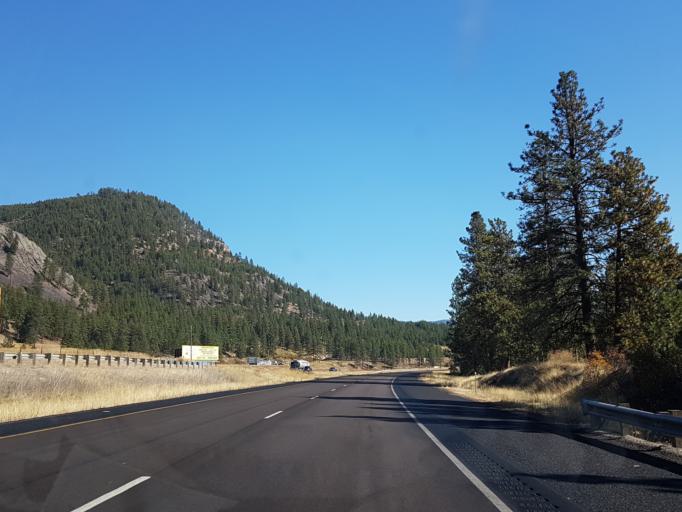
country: US
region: Montana
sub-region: Missoula County
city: Frenchtown
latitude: 47.0179
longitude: -114.5115
